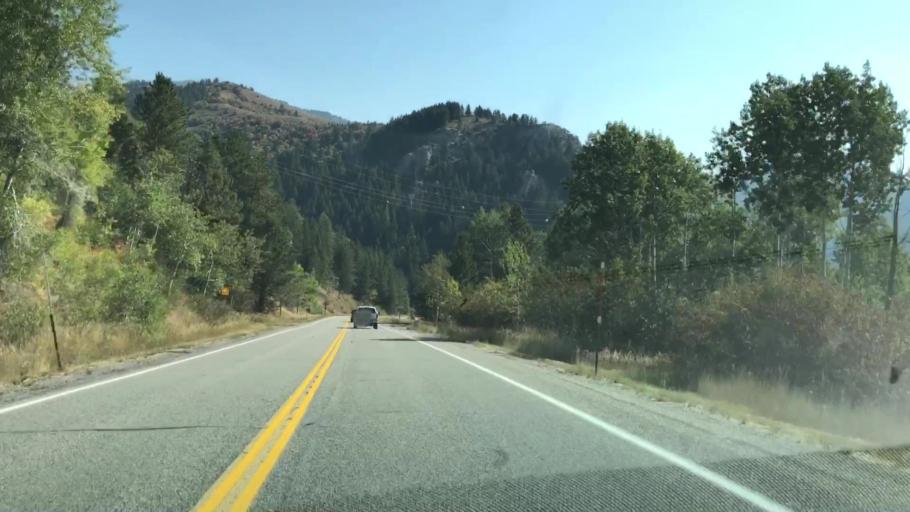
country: US
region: Idaho
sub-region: Teton County
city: Victor
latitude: 43.3191
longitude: -111.1627
